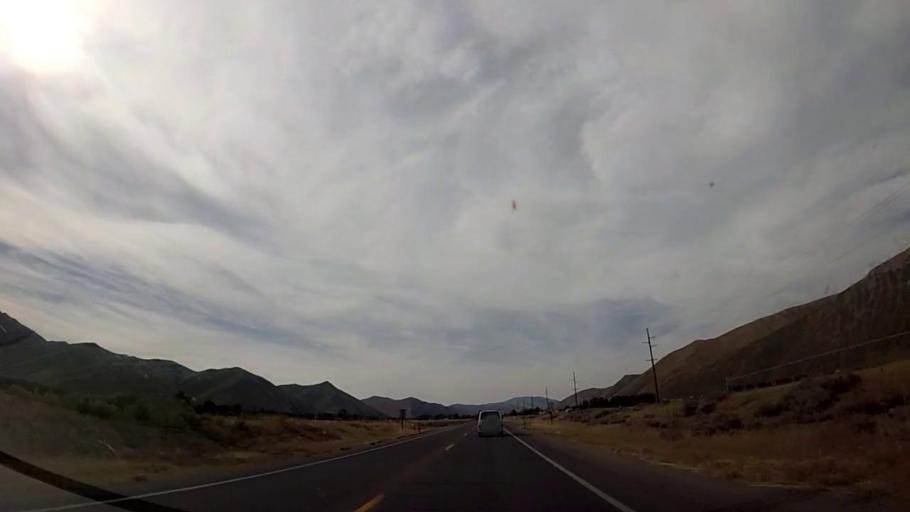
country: US
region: Idaho
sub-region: Blaine County
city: Bellevue
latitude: 43.4790
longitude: -114.2698
